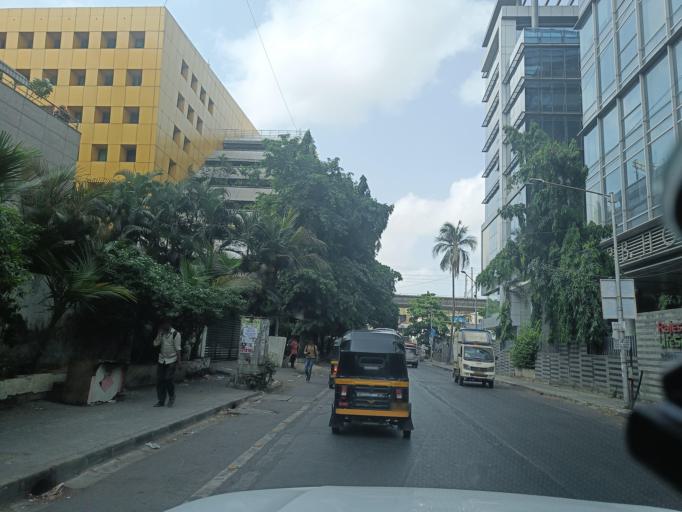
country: IN
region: Maharashtra
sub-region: Mumbai Suburban
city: Powai
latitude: 19.1133
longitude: 72.8671
